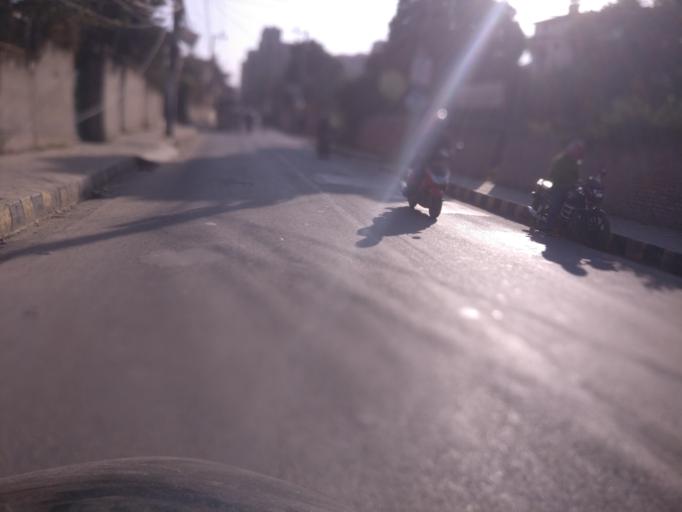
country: NP
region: Central Region
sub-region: Bagmati Zone
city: Patan
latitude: 27.6825
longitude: 85.3063
